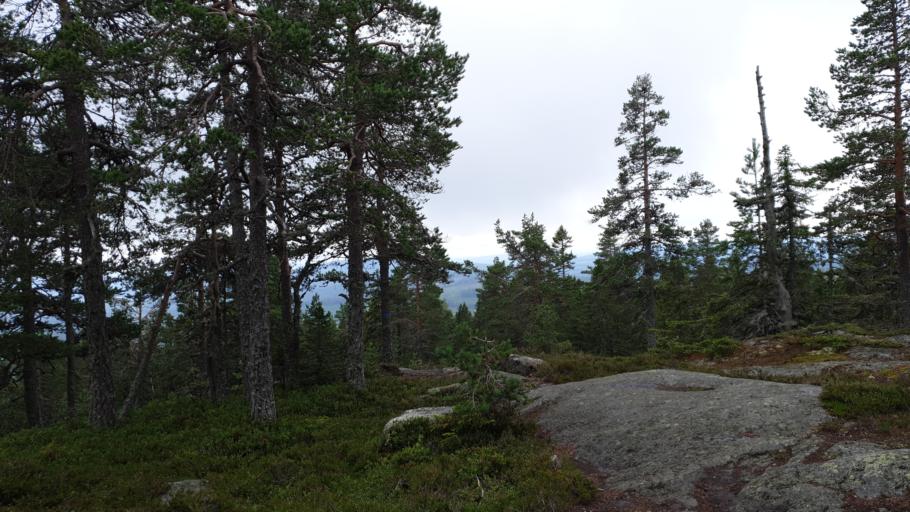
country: SE
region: Gaevleborg
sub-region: Hudiksvalls Kommun
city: Sorforsa
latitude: 61.6429
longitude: 16.7652
